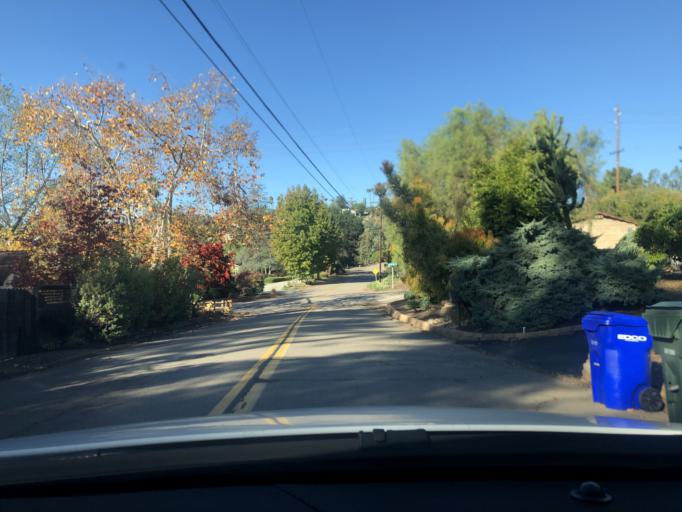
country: US
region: California
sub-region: San Diego County
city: Casa de Oro-Mount Helix
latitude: 32.7635
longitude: -116.9528
